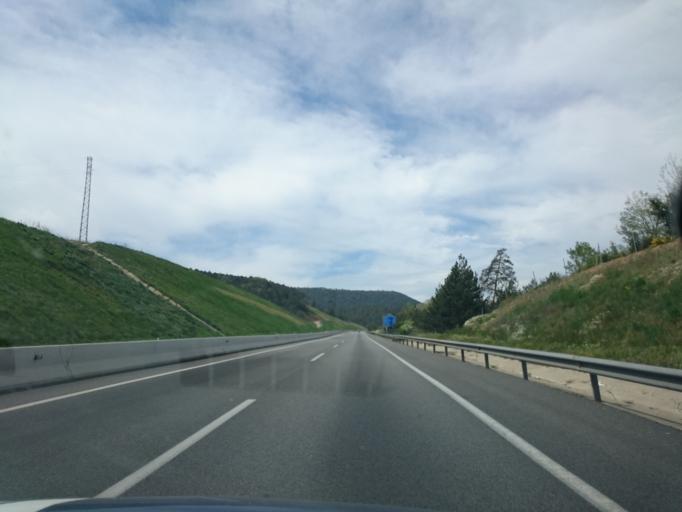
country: ES
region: Catalonia
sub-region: Provincia de Barcelona
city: Muntanyola
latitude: 41.9355
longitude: 2.1730
